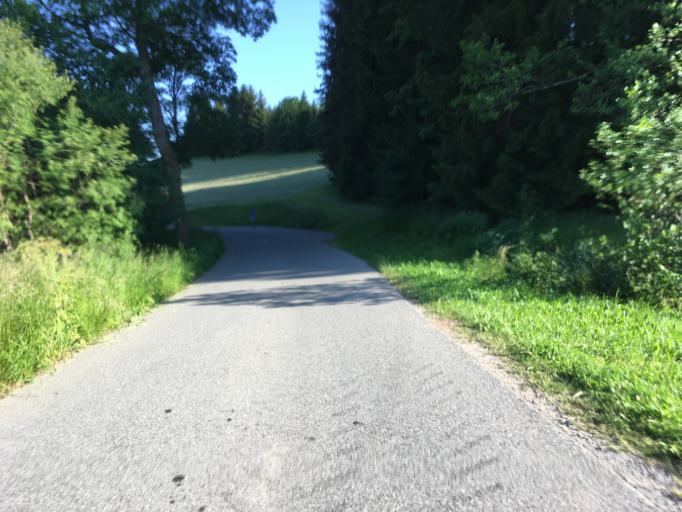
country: DE
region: Baden-Wuerttemberg
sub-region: Freiburg Region
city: Friedenweiler
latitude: 47.9262
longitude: 8.2540
